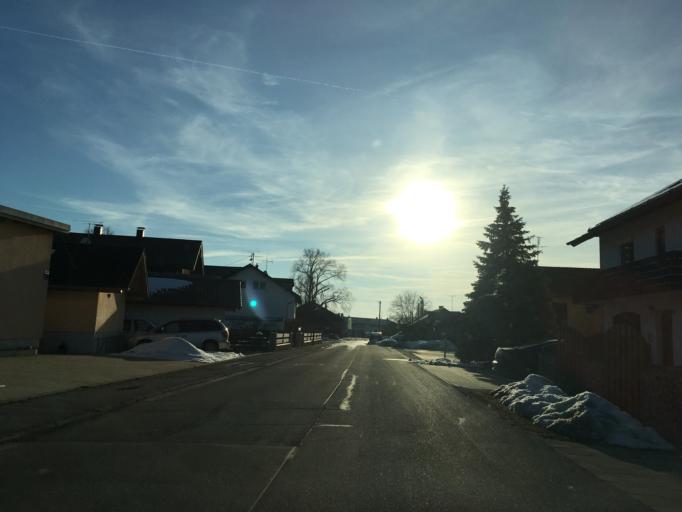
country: DE
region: Bavaria
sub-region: Upper Bavaria
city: Pfaffing
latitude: 48.0833
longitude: 12.0930
